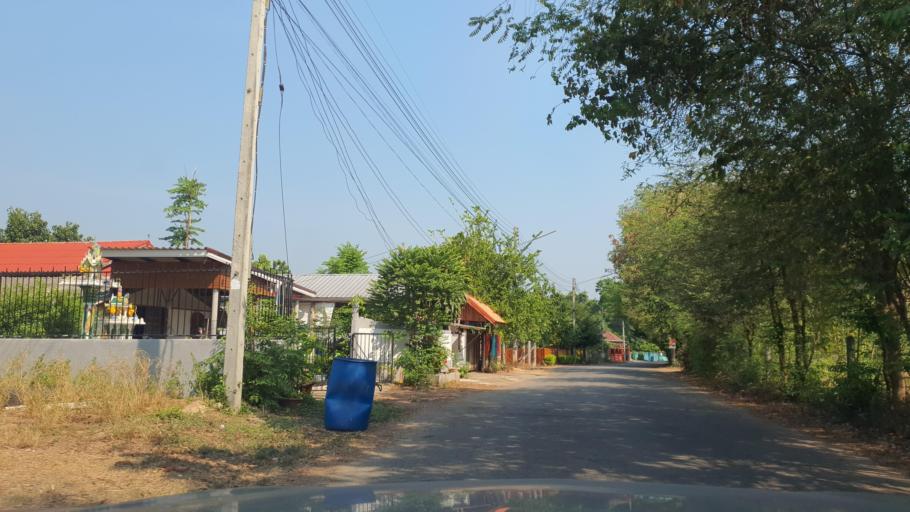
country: TH
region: Kanchanaburi
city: Kanchanaburi
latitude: 14.0692
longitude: 99.4852
